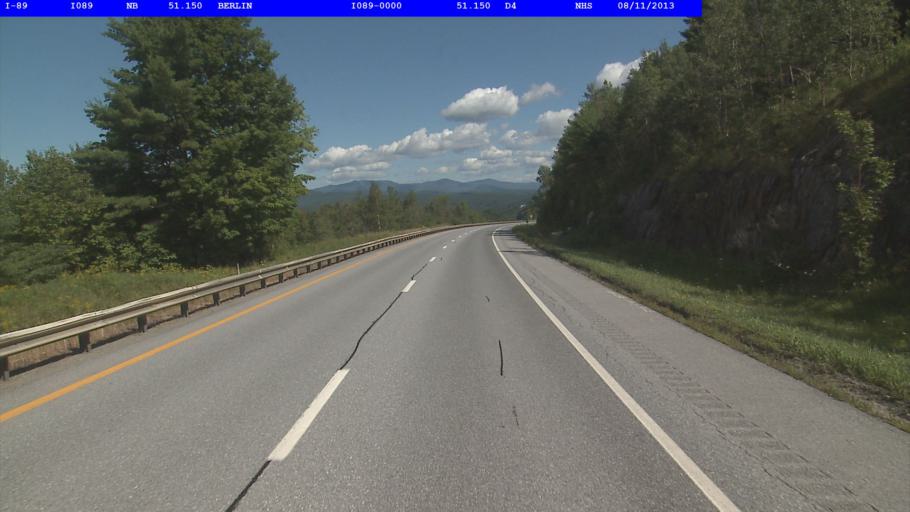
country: US
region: Vermont
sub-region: Washington County
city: Montpelier
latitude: 44.2280
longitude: -72.5861
